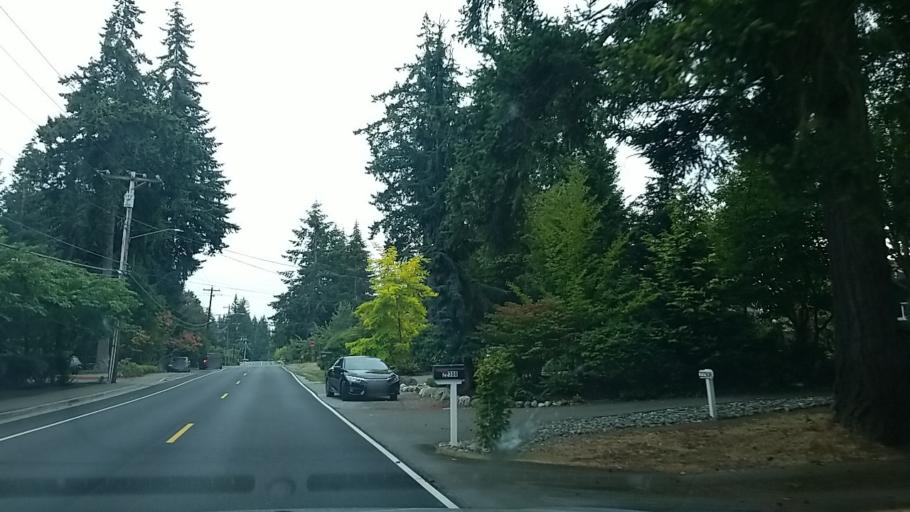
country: US
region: Washington
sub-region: Snohomish County
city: Esperance
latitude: 47.7968
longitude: -122.3598
